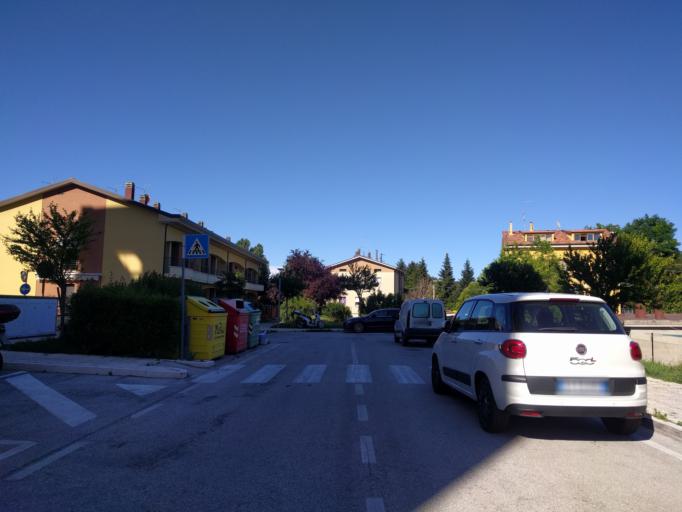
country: IT
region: The Marches
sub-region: Provincia di Pesaro e Urbino
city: Pesaro
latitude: 43.8893
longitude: 12.9102
